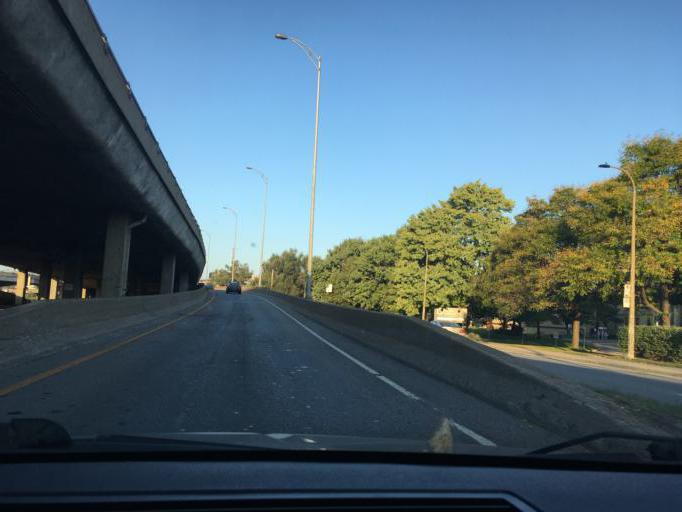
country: CA
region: Quebec
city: Mont-Royal
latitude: 45.5503
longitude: -73.6314
